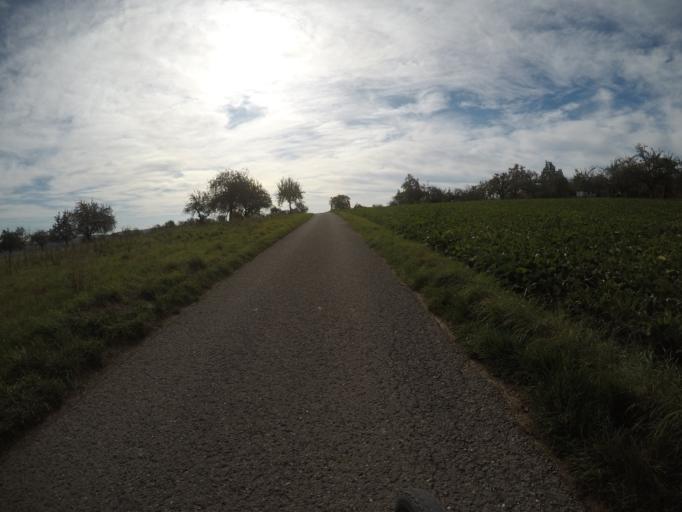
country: DE
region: Baden-Wuerttemberg
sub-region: Regierungsbezirk Stuttgart
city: Gartringen
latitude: 48.6552
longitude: 8.9058
